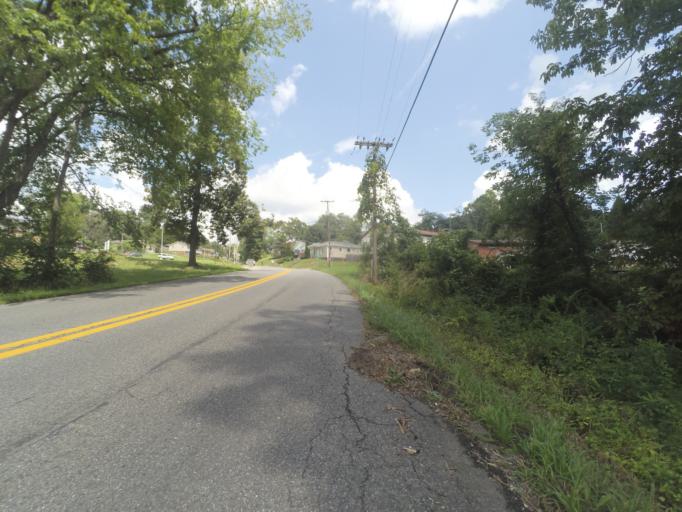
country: US
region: West Virginia
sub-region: Cabell County
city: Pea Ridge
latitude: 38.4086
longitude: -82.3714
